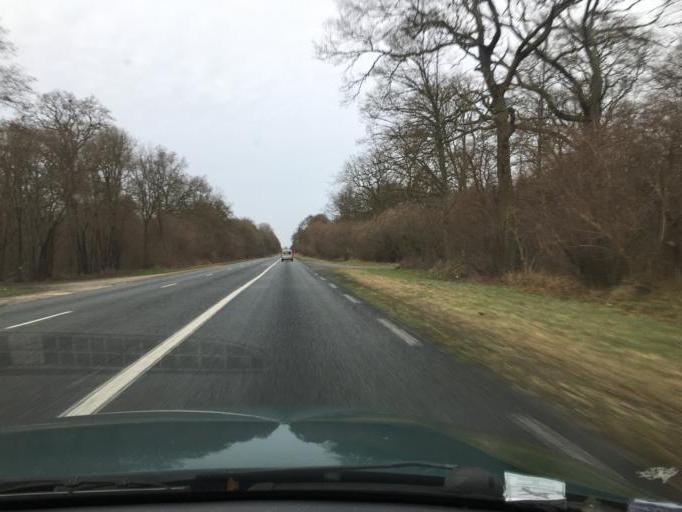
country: FR
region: Picardie
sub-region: Departement de l'Oise
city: Senlis
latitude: 49.1802
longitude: 2.5664
